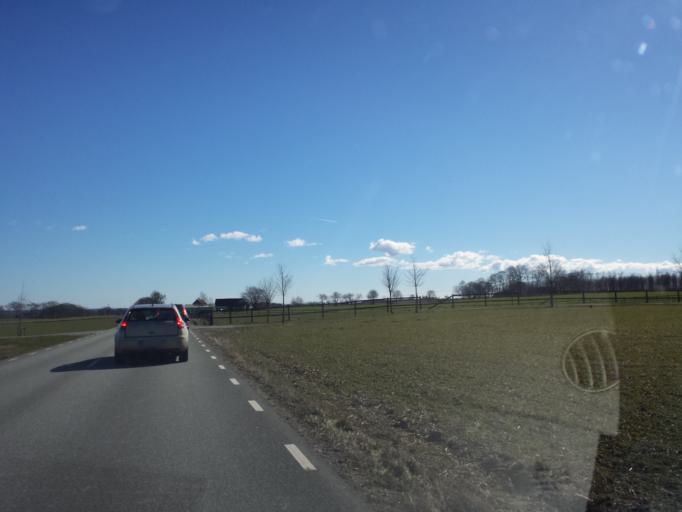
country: SE
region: Skane
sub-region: Sjobo Kommun
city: Sjoebo
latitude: 55.6132
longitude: 13.7918
